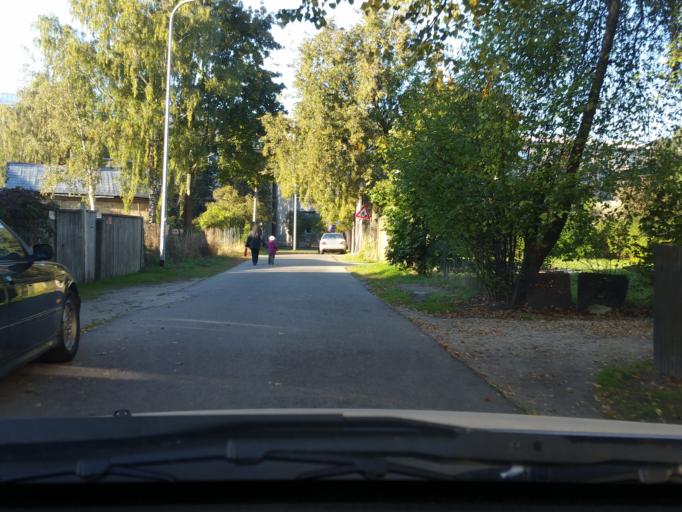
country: LV
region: Riga
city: Jaunciems
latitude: 56.9814
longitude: 24.1869
